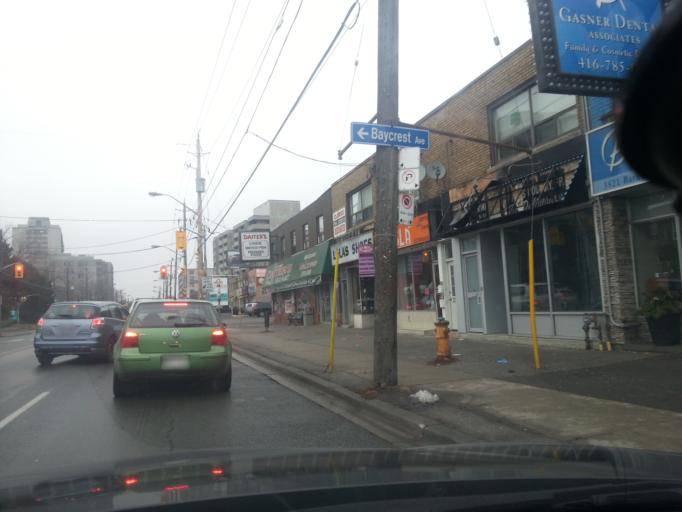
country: CA
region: Ontario
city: Toronto
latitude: 43.7292
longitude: -79.4320
